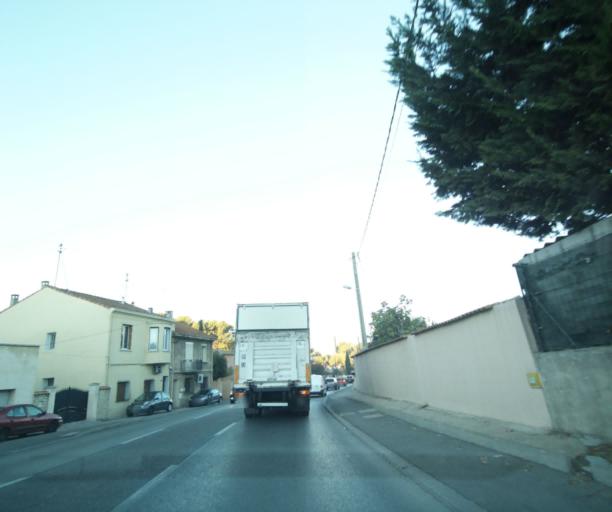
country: FR
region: Provence-Alpes-Cote d'Azur
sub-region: Departement des Bouches-du-Rhone
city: Marseille 12
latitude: 43.3232
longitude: 5.4468
